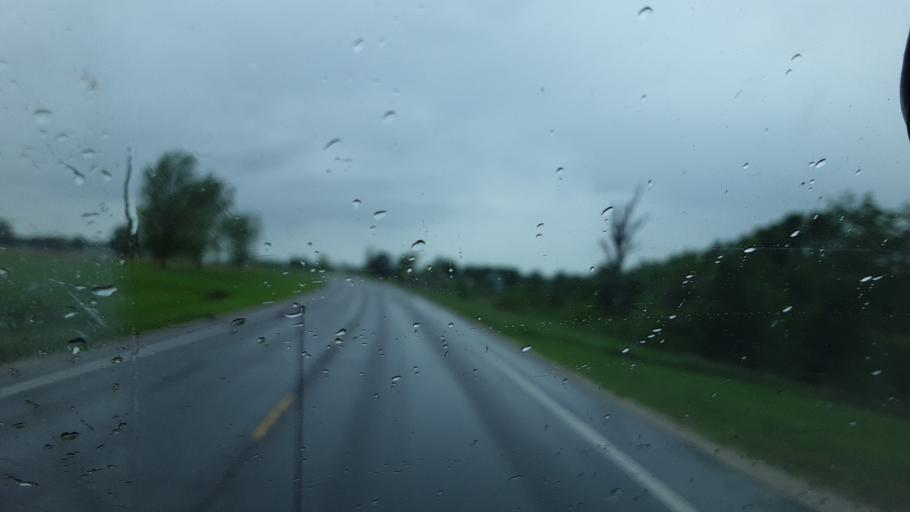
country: US
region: Missouri
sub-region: Monroe County
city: Paris
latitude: 39.4797
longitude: -92.1081
